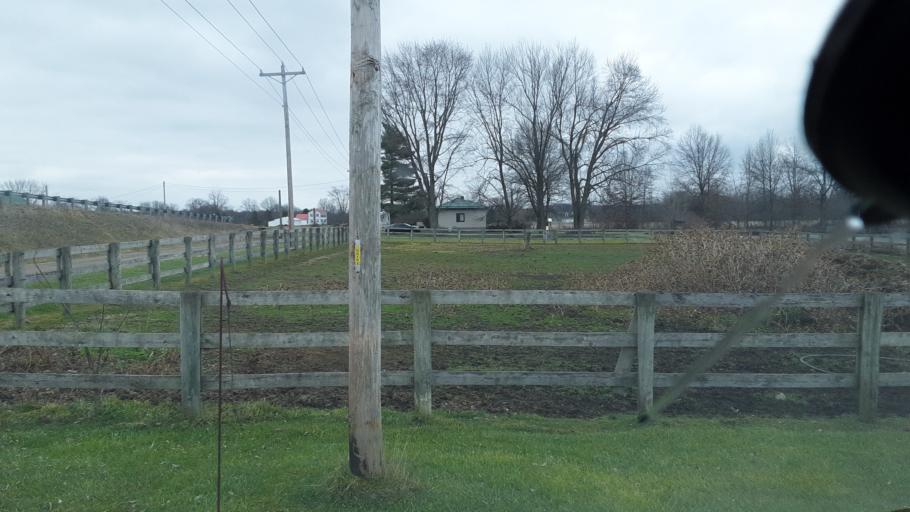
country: US
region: Ohio
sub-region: Delaware County
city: Sunbury
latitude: 40.3251
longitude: -82.8957
